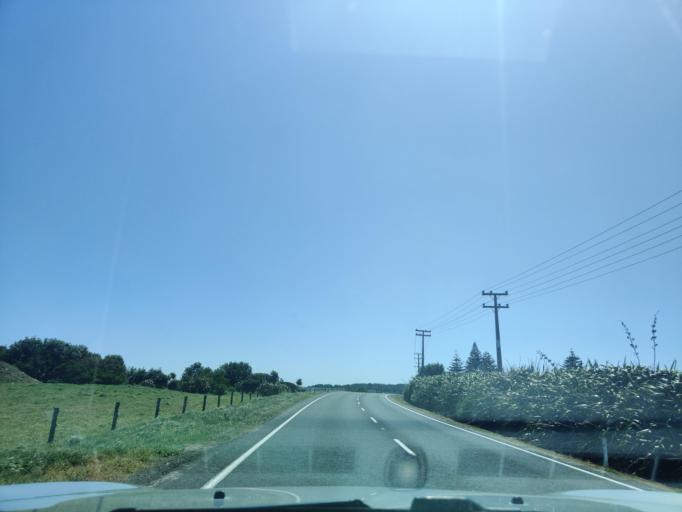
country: NZ
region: Taranaki
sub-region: South Taranaki District
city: Opunake
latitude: -39.4391
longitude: 173.8345
